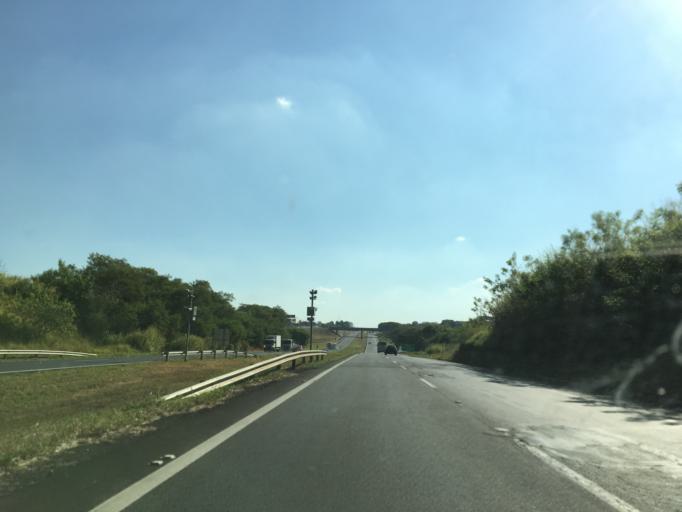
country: BR
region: Sao Paulo
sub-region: Piracicaba
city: Piracicaba
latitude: -22.7234
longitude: -47.5891
